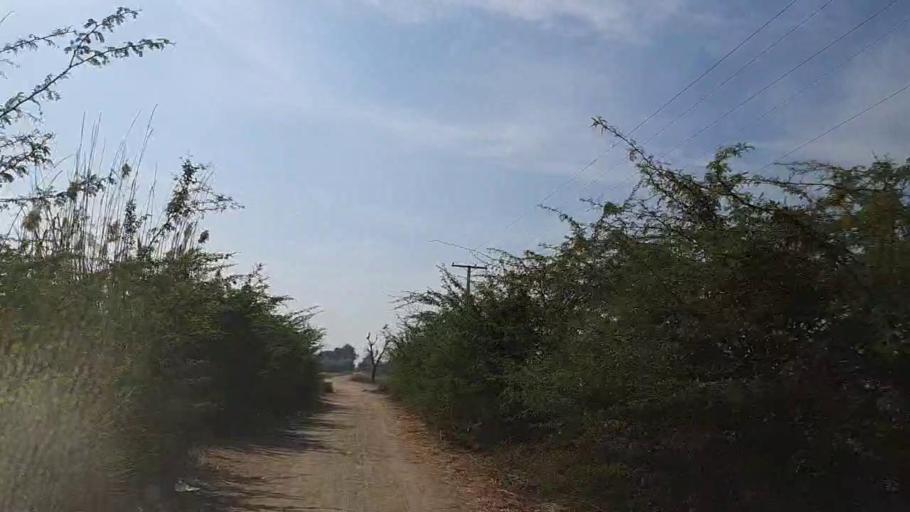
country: PK
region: Sindh
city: Mirpur Khas
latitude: 25.4720
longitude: 68.9745
